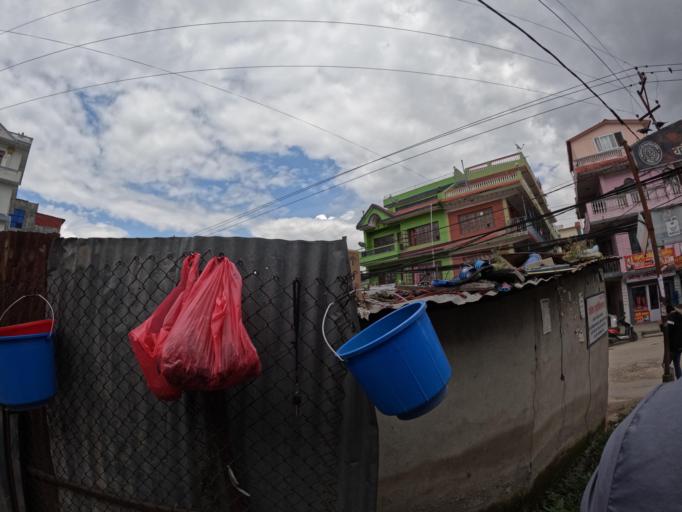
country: NP
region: Central Region
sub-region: Bagmati Zone
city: Kathmandu
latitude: 27.7406
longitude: 85.3212
